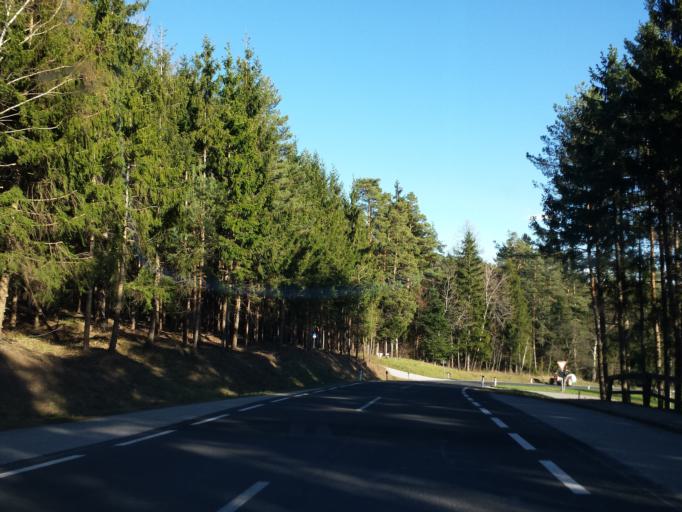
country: AT
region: Styria
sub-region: Politischer Bezirk Graz-Umgebung
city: Sankt Radegund bei Graz
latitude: 47.1563
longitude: 15.4865
